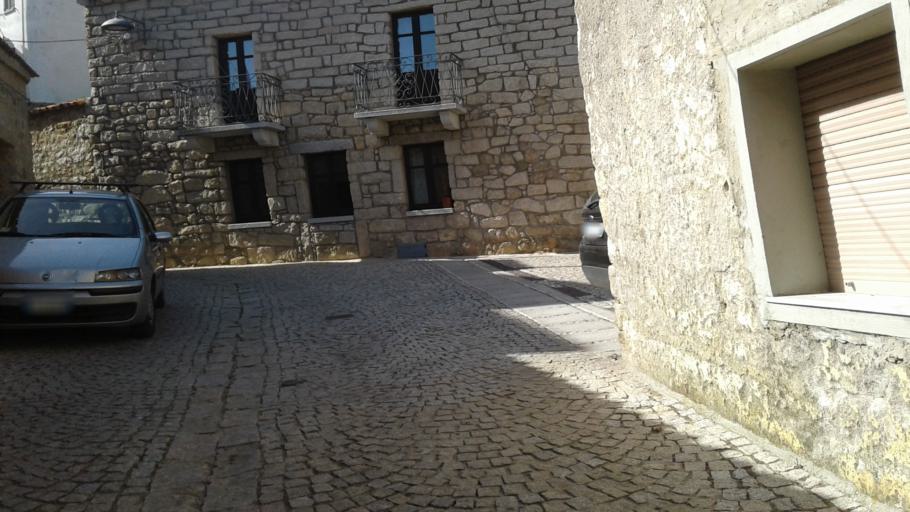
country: IT
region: Sardinia
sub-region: Provincia di Olbia-Tempio
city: Aggius
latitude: 40.9287
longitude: 9.0656
